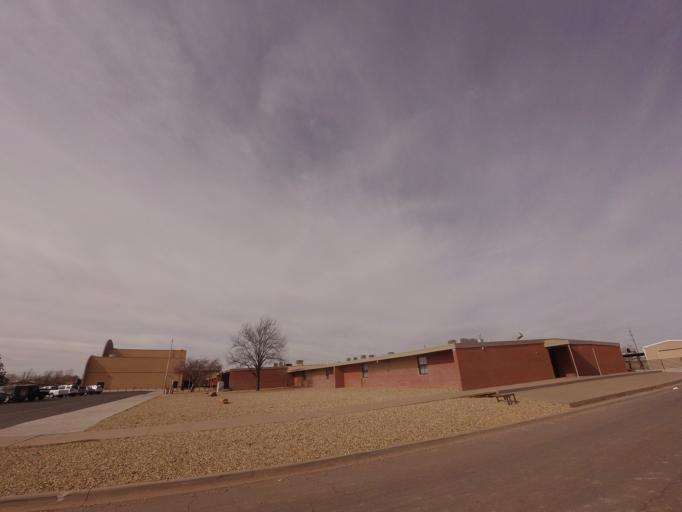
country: US
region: New Mexico
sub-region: Curry County
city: Clovis
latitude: 34.4103
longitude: -103.2404
